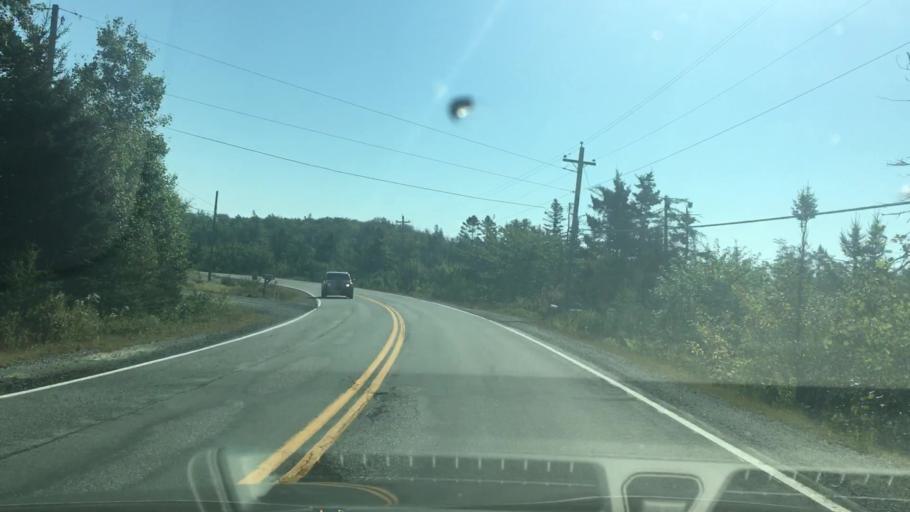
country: CA
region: Nova Scotia
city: Cole Harbour
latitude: 44.7752
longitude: -63.0540
